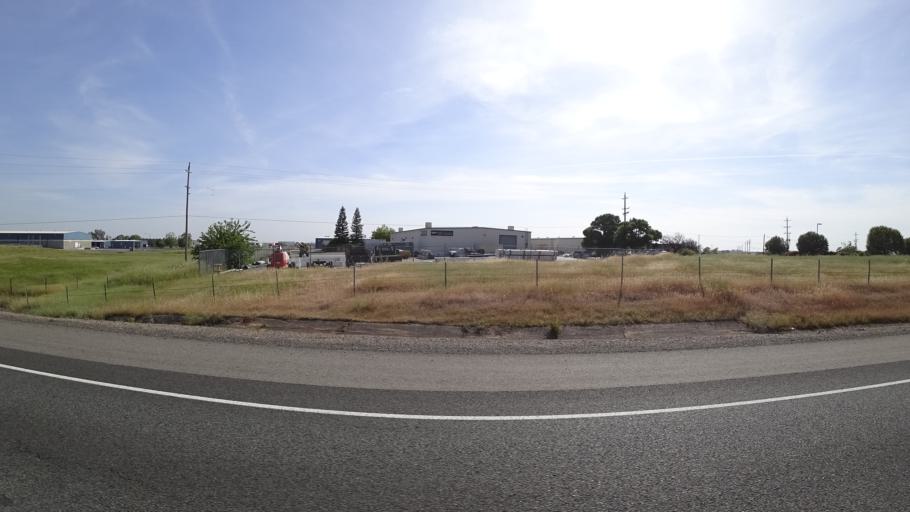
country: US
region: California
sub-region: Butte County
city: Durham
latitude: 39.6470
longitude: -121.7219
